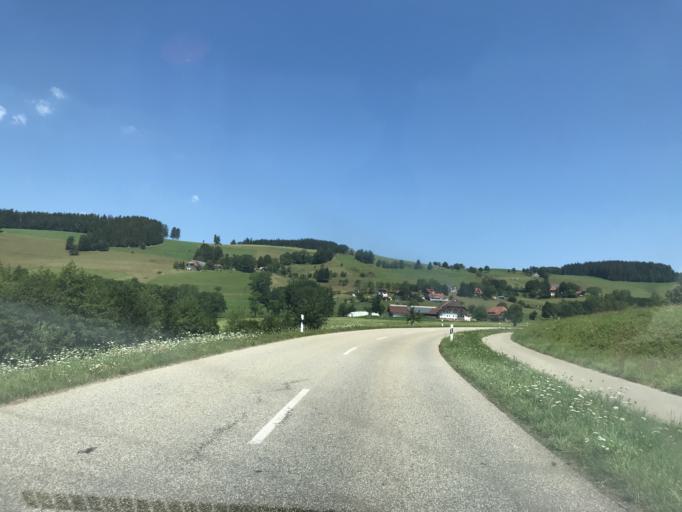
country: DE
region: Baden-Wuerttemberg
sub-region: Freiburg Region
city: Sankt Peter
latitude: 48.0183
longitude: 8.0427
